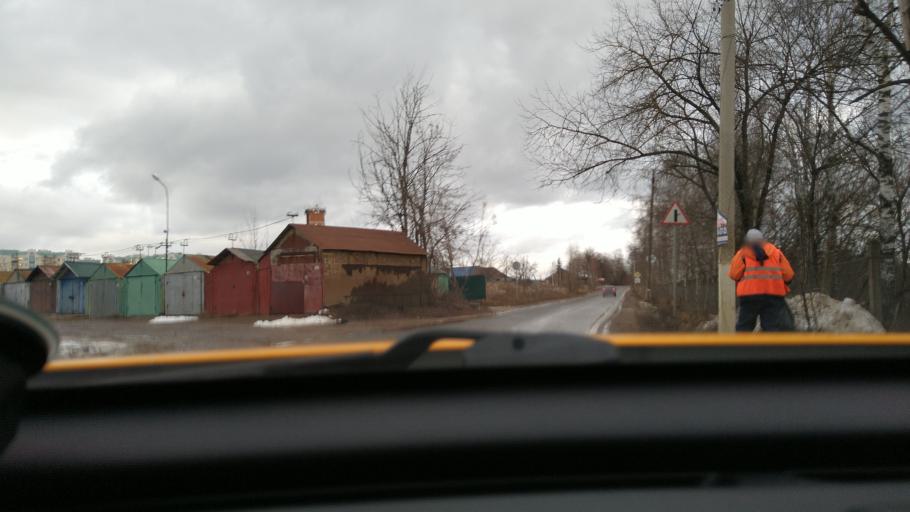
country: RU
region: Moskovskaya
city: Petrovo-Dal'neye
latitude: 55.7688
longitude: 37.2212
